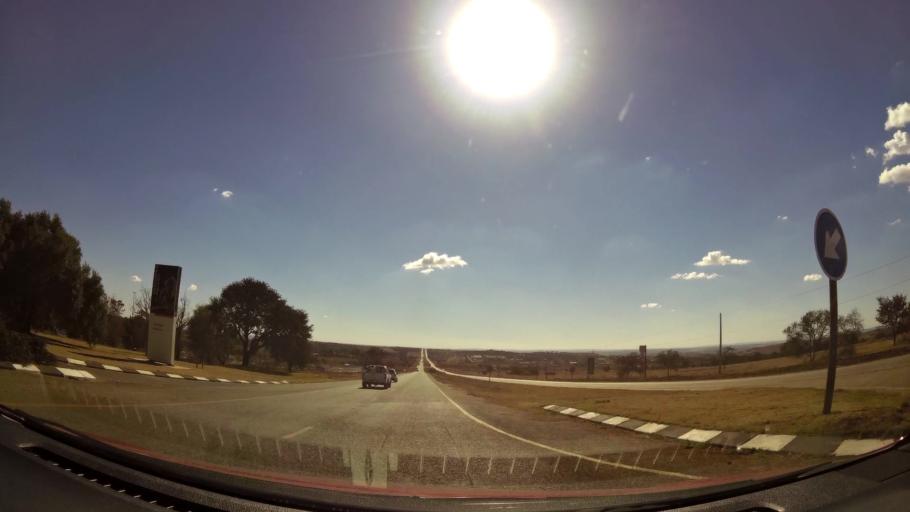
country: ZA
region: Gauteng
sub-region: West Rand District Municipality
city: Carletonville
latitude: -26.4129
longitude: 27.4326
